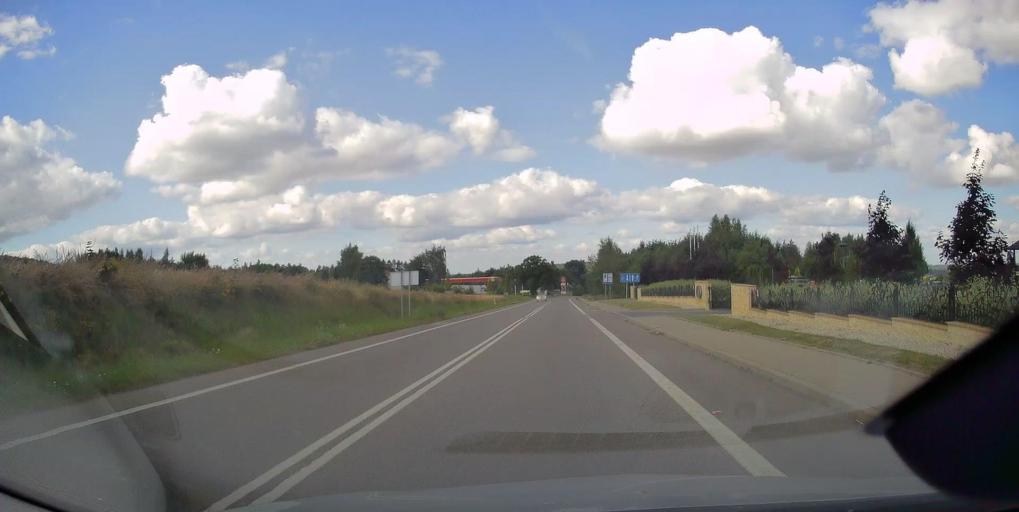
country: PL
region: Swietokrzyskie
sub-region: Powiat kielecki
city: Nowa Slupia
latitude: 50.8528
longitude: 21.0853
